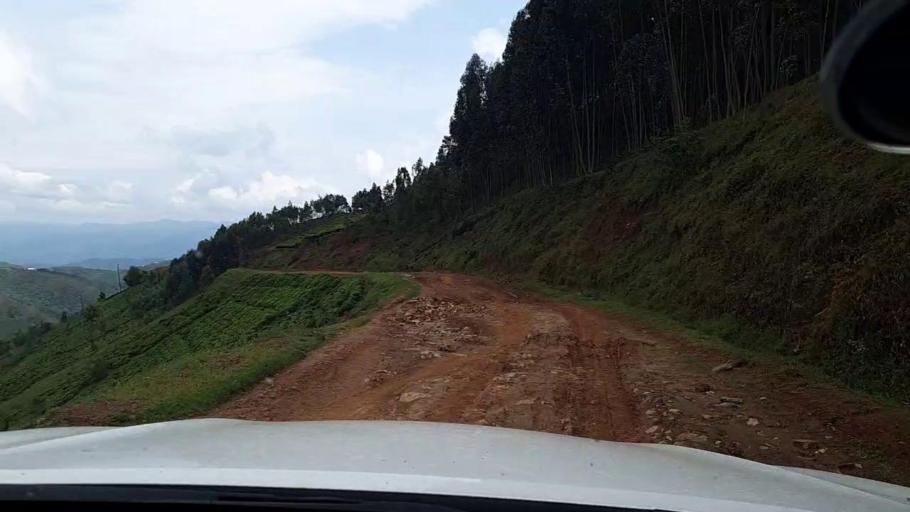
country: RW
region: Western Province
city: Kibuye
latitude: -2.1669
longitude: 29.3990
